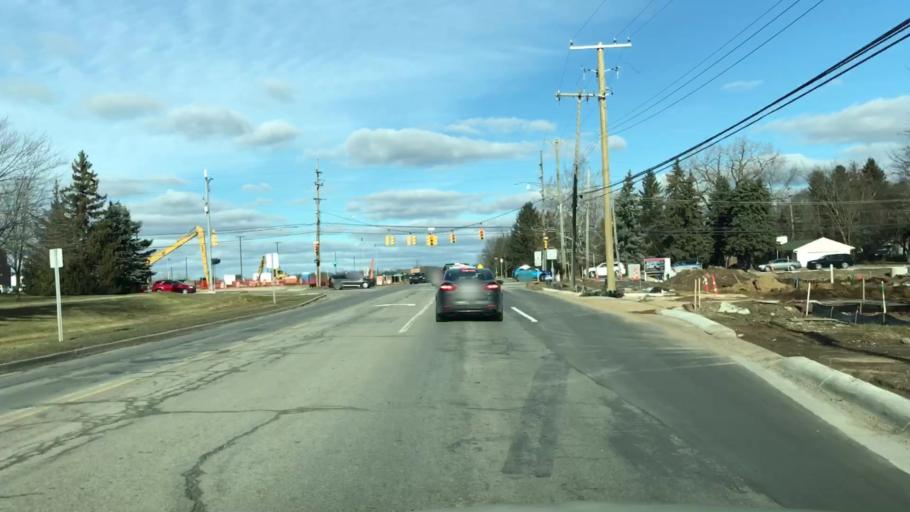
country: US
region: Michigan
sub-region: Oakland County
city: Auburn Hills
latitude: 42.6934
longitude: -83.1945
